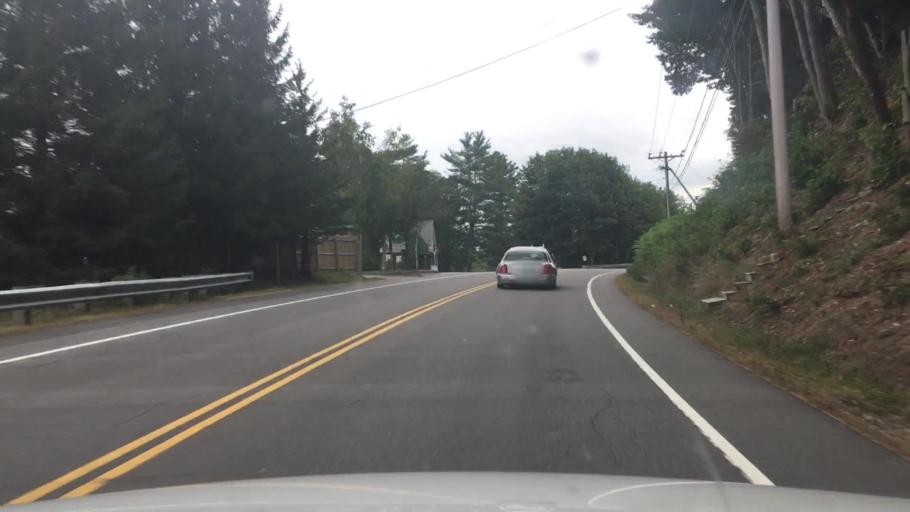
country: US
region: New Hampshire
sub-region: Strafford County
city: New Durham
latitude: 43.4823
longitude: -71.2419
